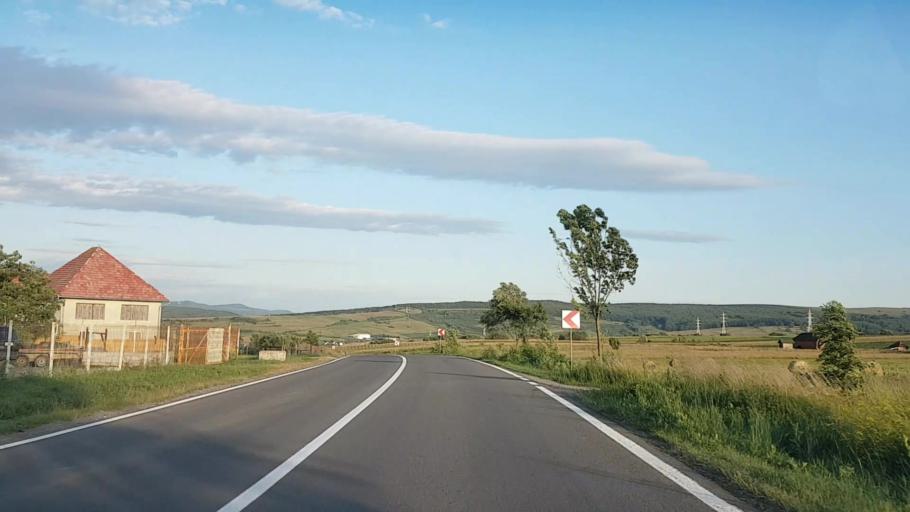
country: RO
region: Harghita
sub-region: Comuna Lupeni
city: Lupeni
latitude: 46.3734
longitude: 25.2204
